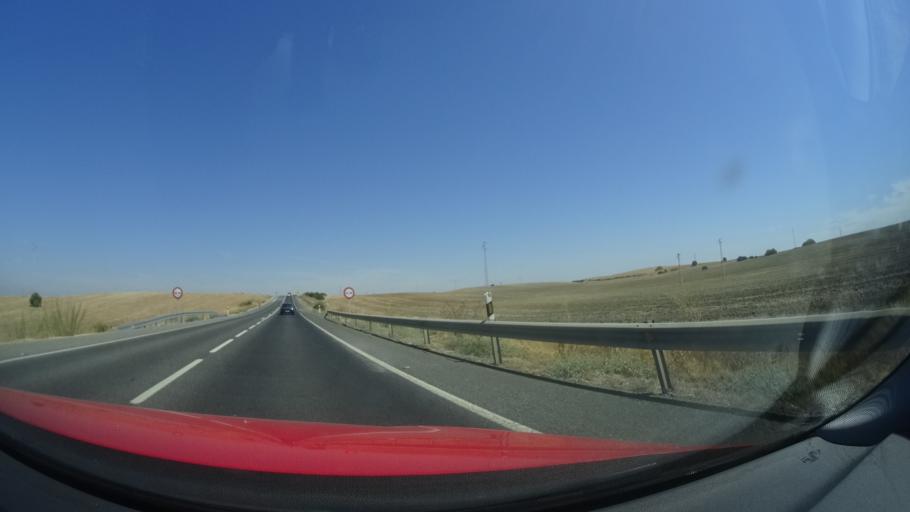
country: ES
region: Andalusia
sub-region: Provincia de Sevilla
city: Las Cabezas de San Juan
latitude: 36.9367
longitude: -5.9201
